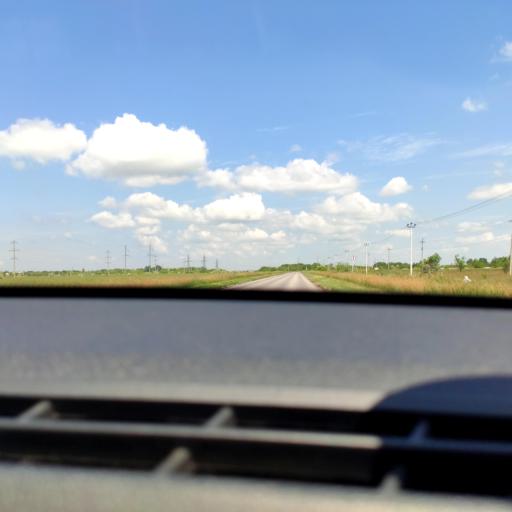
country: RU
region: Samara
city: Podstepki
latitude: 53.5601
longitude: 49.0920
